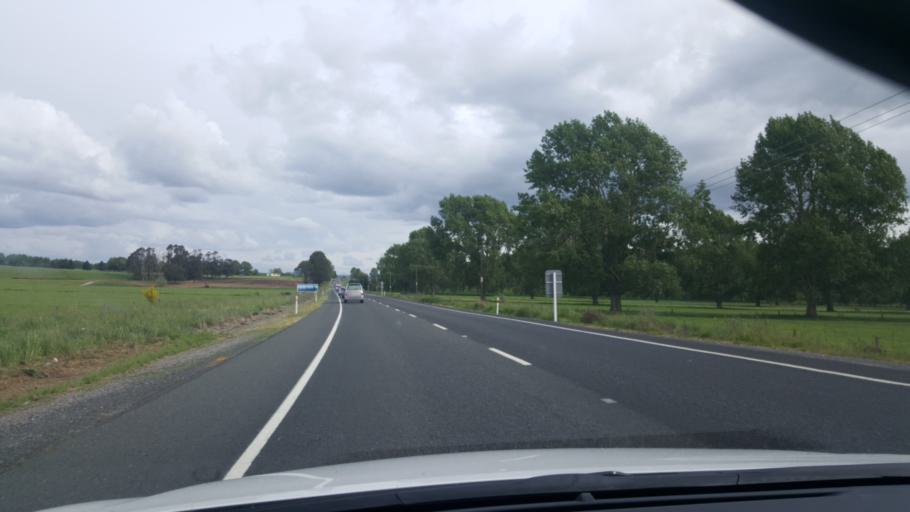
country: NZ
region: Waikato
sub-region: Taupo District
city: Taupo
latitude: -38.4879
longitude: 176.2906
